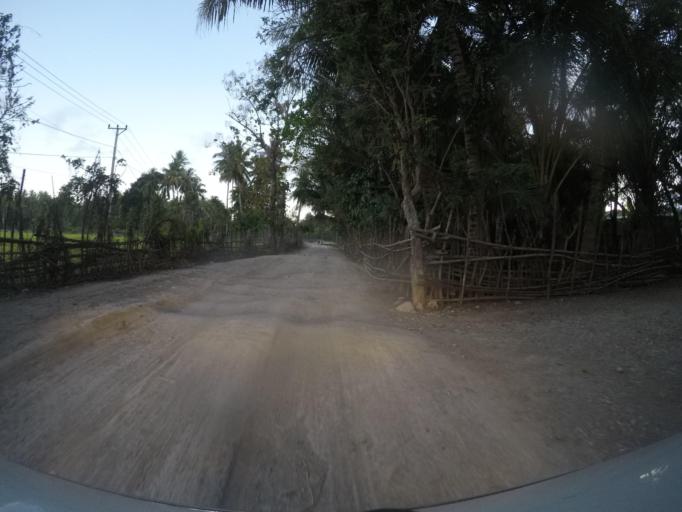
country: TL
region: Viqueque
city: Viqueque
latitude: -8.7787
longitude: 126.6367
